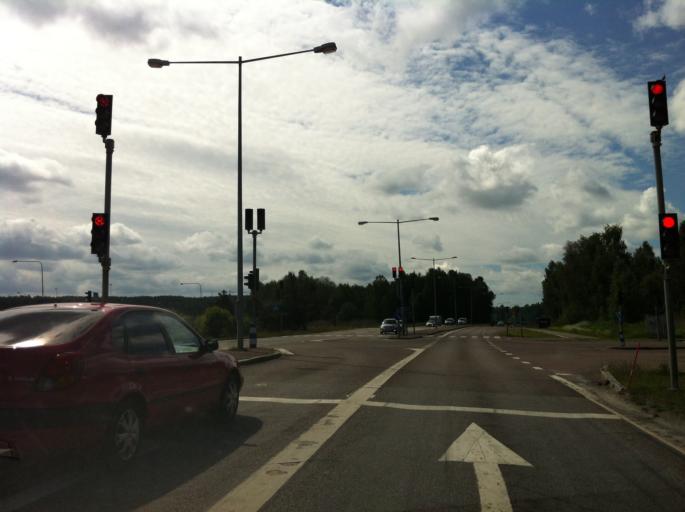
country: SE
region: Vaermland
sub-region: Grums Kommun
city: Grums
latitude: 59.3421
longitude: 13.1097
